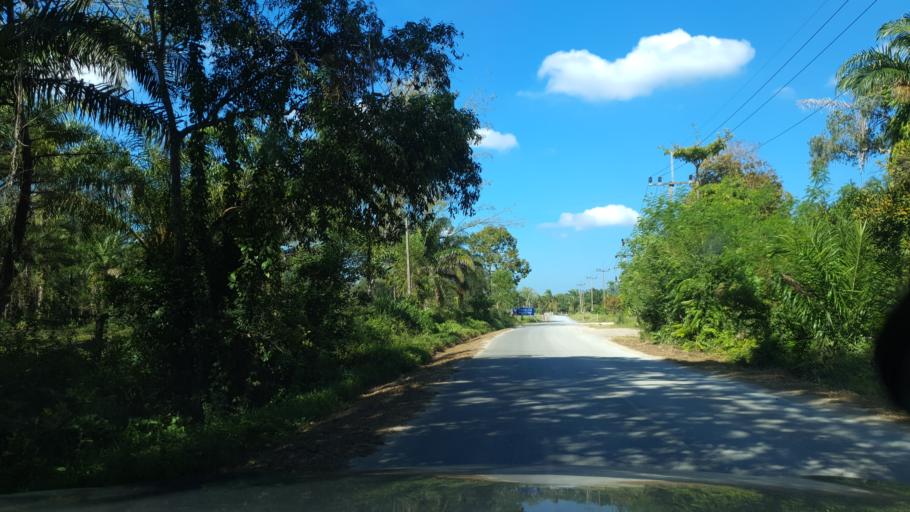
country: TH
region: Phangnga
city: Ban Ao Nang
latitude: 8.0494
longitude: 98.8025
